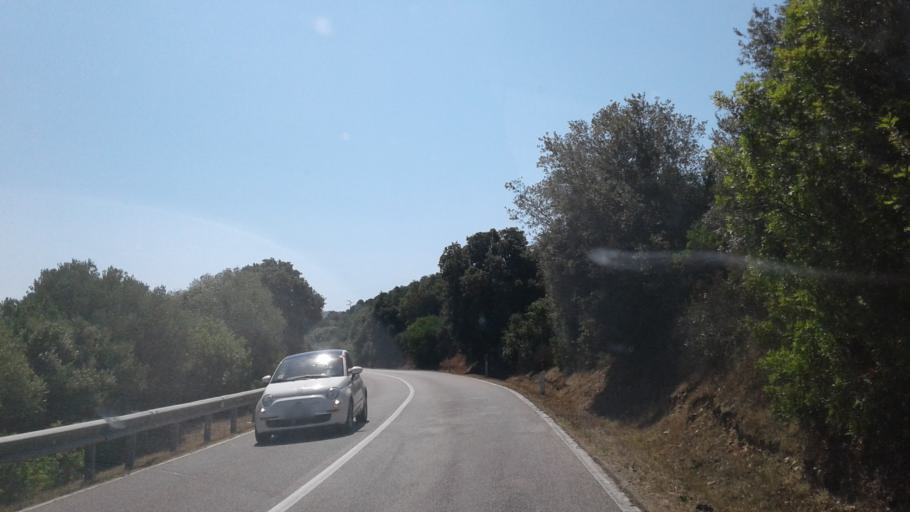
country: IT
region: Sardinia
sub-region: Provincia di Olbia-Tempio
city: Palau
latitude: 41.1709
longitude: 9.3255
